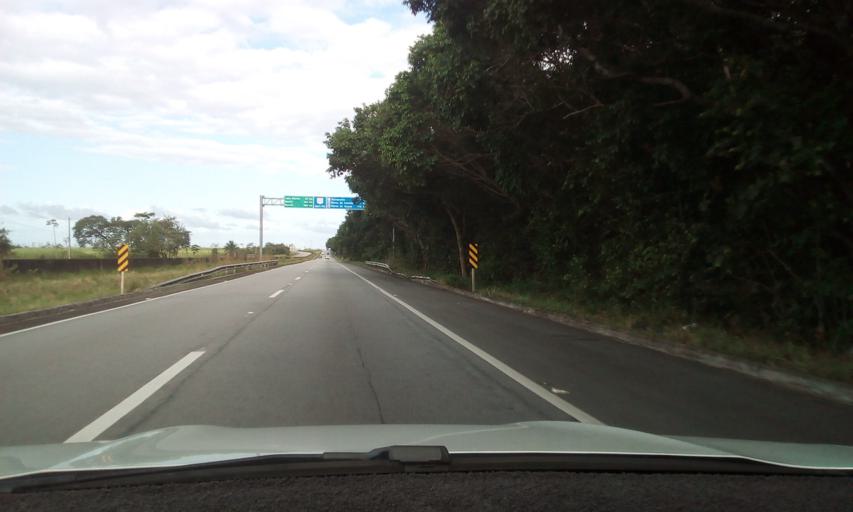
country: BR
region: Paraiba
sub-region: Santa Rita
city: Santa Rita
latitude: -7.0749
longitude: -34.9932
